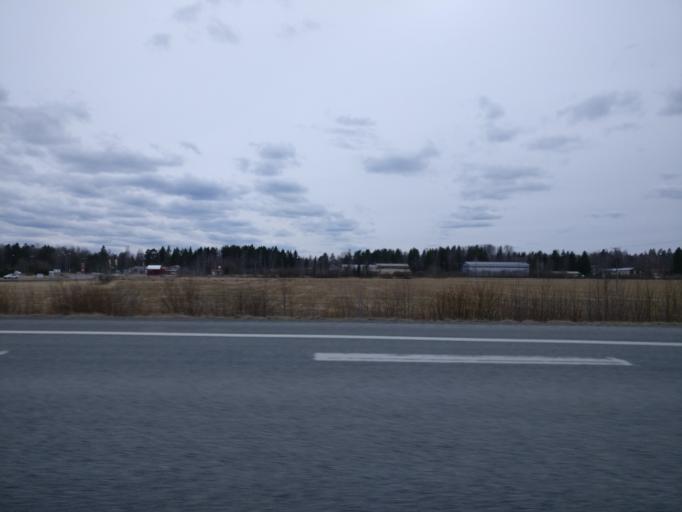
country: FI
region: Haeme
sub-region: Haemeenlinna
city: Kalvola
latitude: 61.0998
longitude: 24.1614
